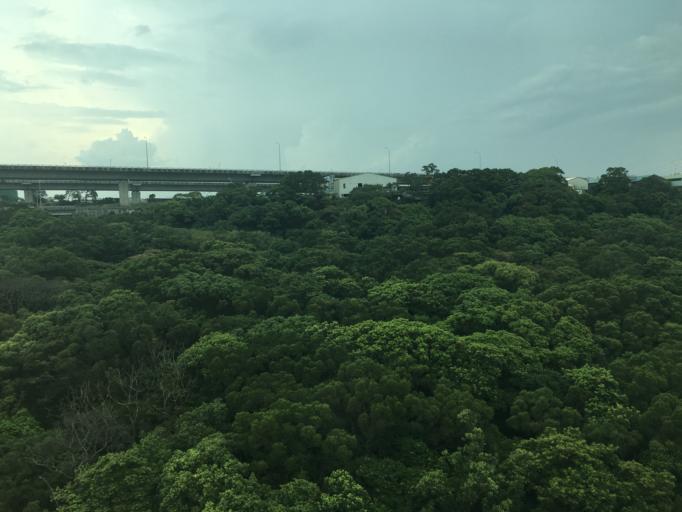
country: TW
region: Taiwan
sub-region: Taoyuan
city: Taoyuan
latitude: 25.0680
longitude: 121.3487
